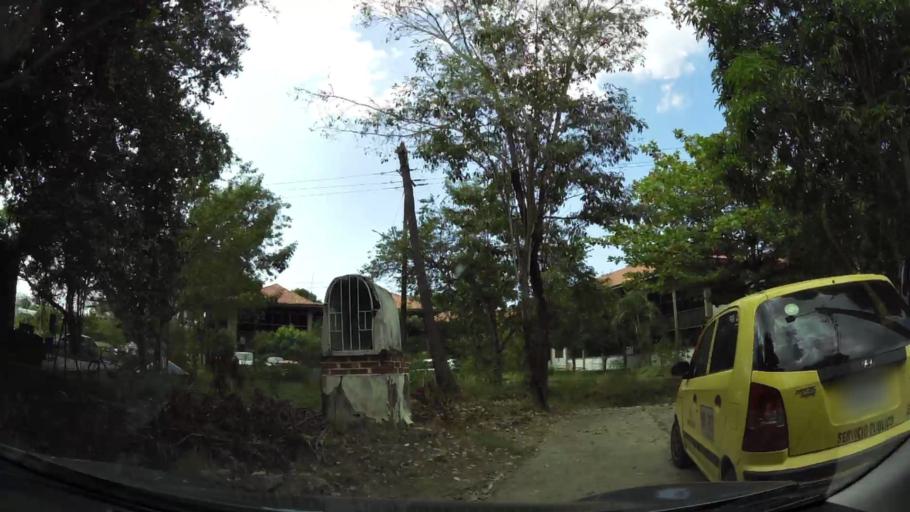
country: CO
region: Bolivar
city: Cartagena
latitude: 10.3729
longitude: -75.4607
